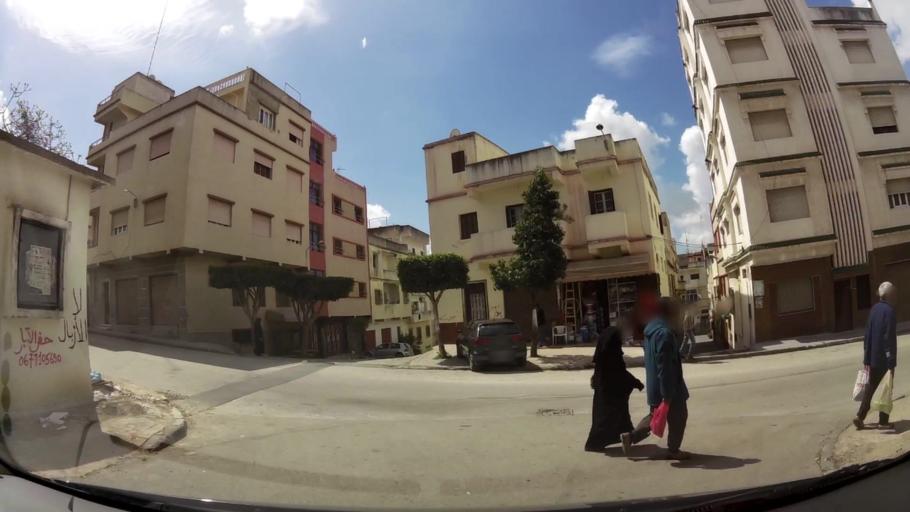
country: MA
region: Tanger-Tetouan
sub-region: Tanger-Assilah
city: Tangier
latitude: 35.7591
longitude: -5.8187
